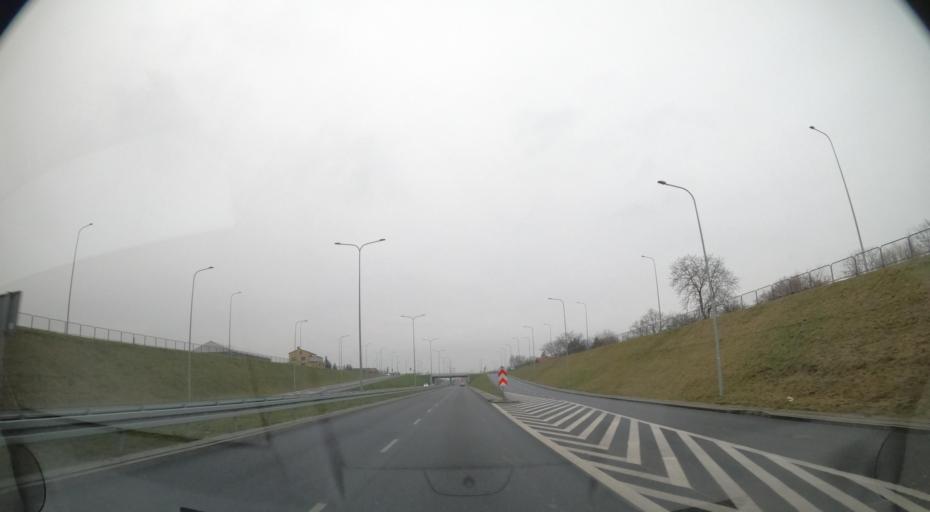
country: PL
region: Masovian Voivodeship
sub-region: Radom
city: Radom
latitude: 51.3989
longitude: 21.1984
